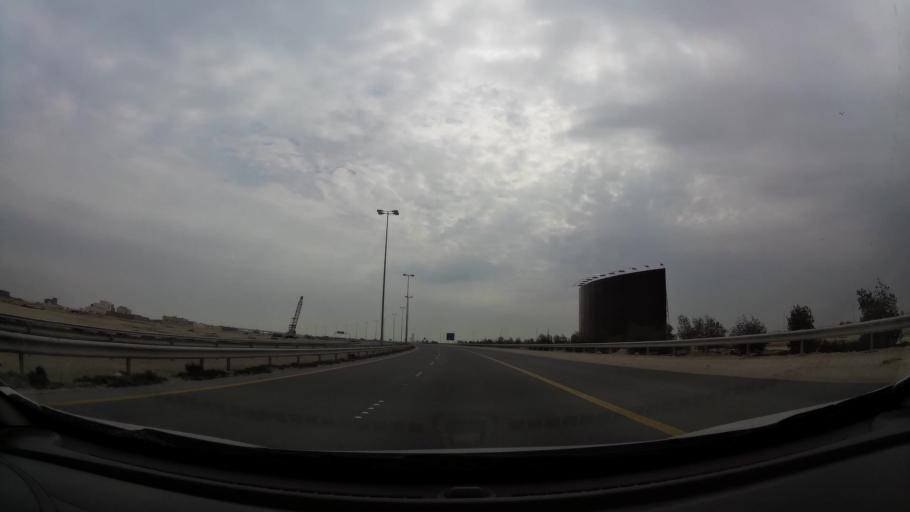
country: BH
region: Northern
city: Ar Rifa'
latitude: 26.0587
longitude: 50.6080
